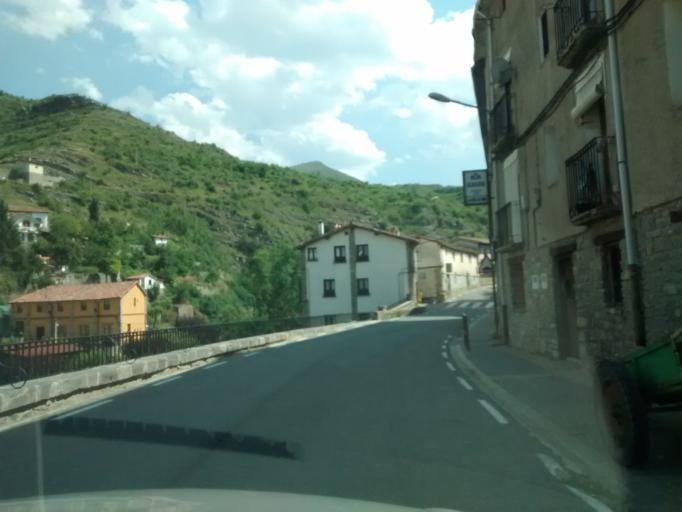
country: ES
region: La Rioja
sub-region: Provincia de La Rioja
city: Soto en Cameros
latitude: 42.2863
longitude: -2.4267
